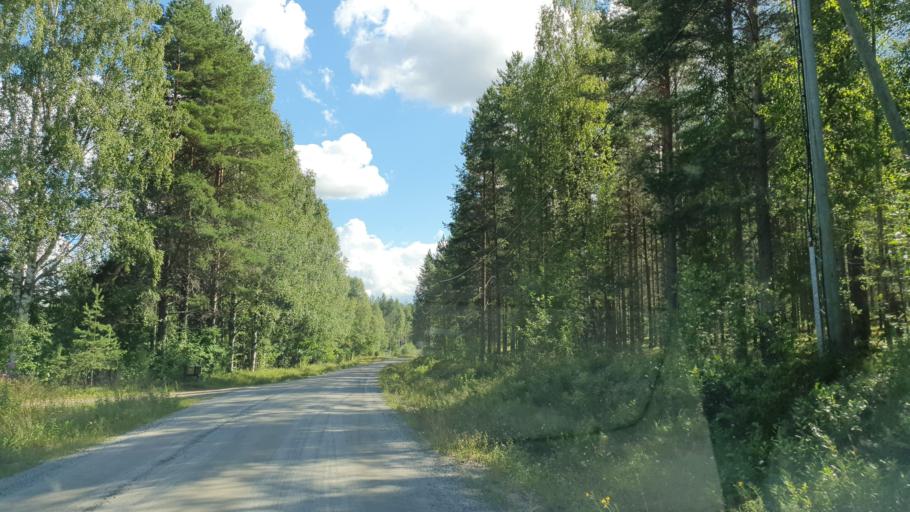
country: FI
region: Kainuu
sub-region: Kehys-Kainuu
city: Kuhmo
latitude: 64.1023
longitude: 29.4023
